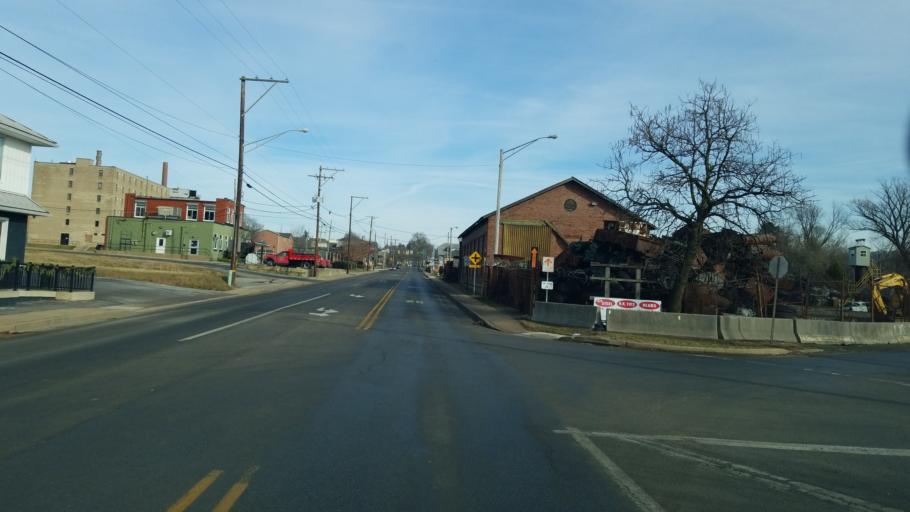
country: US
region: Pennsylvania
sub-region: Indiana County
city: Indiana
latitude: 40.6121
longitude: -79.1586
